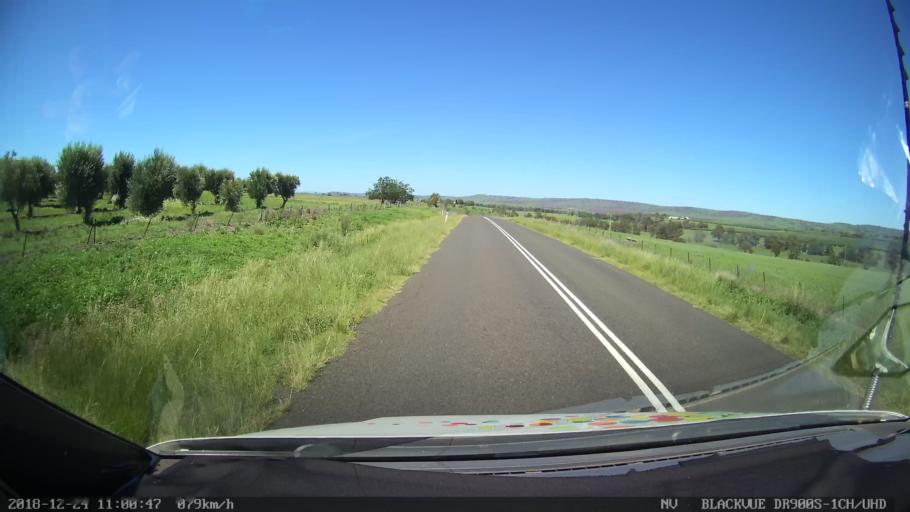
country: AU
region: New South Wales
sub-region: Upper Hunter Shire
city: Merriwa
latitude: -32.0710
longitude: 150.3912
